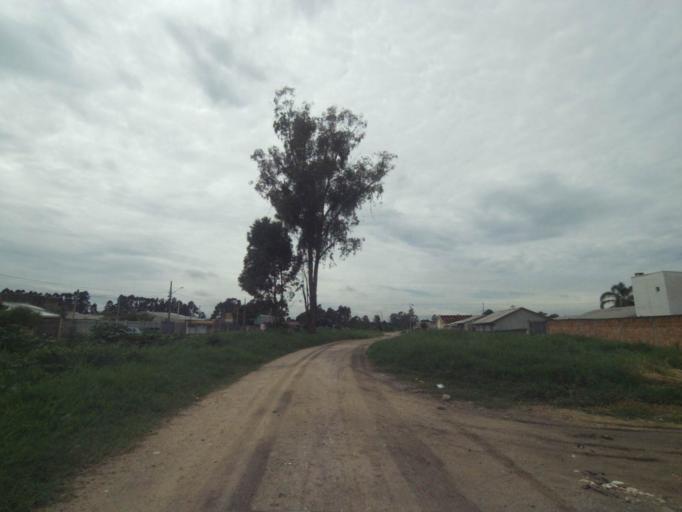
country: BR
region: Parana
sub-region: Pinhais
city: Pinhais
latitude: -25.4734
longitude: -49.1906
